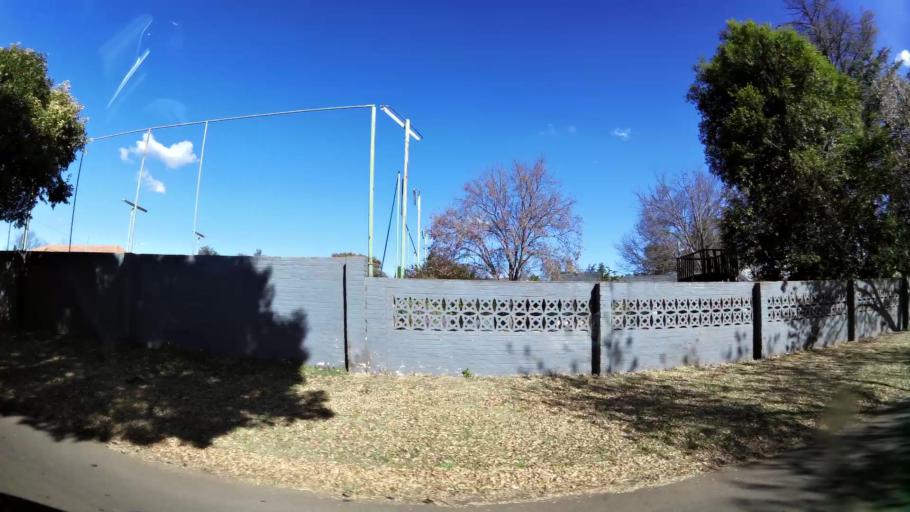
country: ZA
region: Gauteng
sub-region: West Rand District Municipality
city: Carletonville
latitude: -26.3708
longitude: 27.4061
